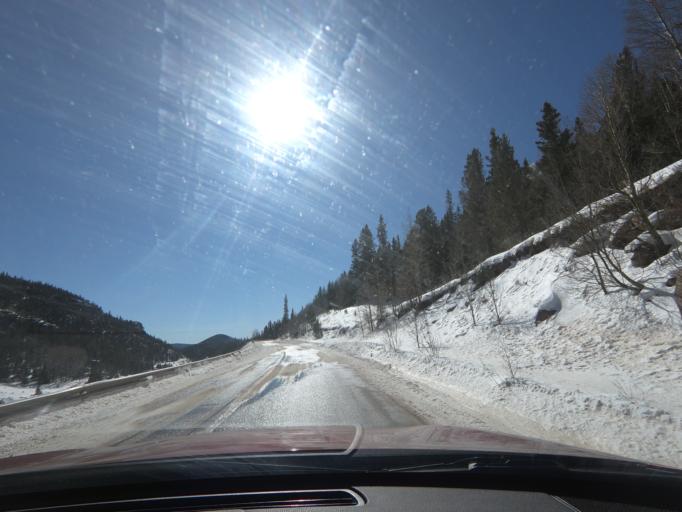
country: US
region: Colorado
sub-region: Teller County
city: Cripple Creek
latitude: 38.7523
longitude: -105.1028
